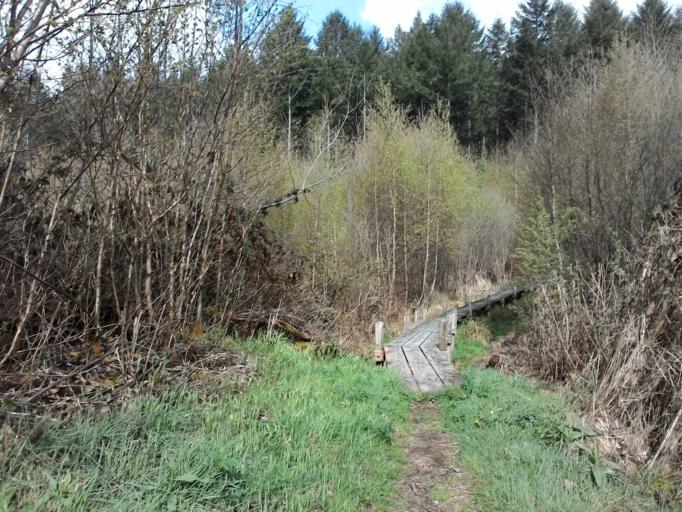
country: FR
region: Bourgogne
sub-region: Departement de la Cote-d'Or
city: Saulieu
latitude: 47.2499
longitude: 4.1841
